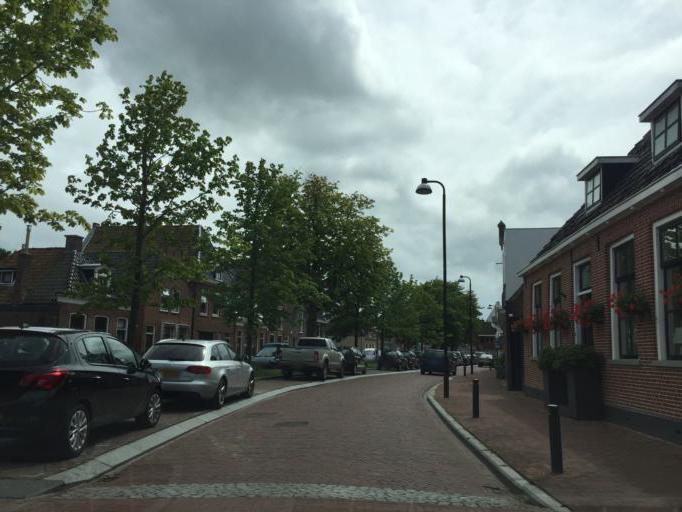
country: NL
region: Friesland
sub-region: Gemeente Dongeradeel
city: Dokkum
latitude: 53.3271
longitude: 6.0010
